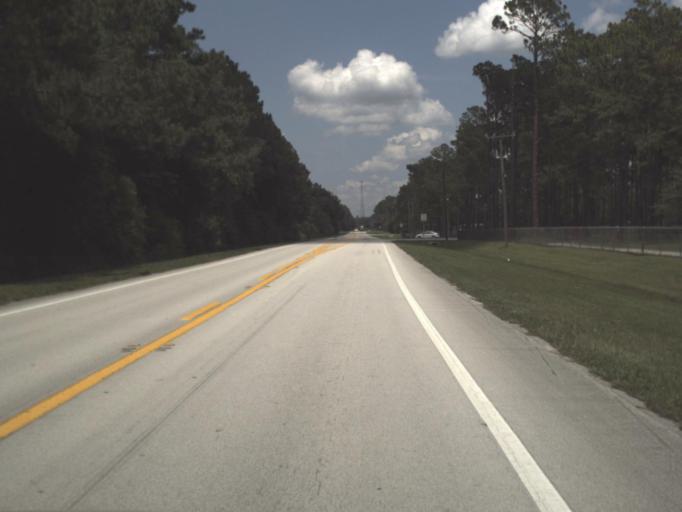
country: US
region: Florida
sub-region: Baker County
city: Macclenny
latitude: 30.2388
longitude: -82.1367
